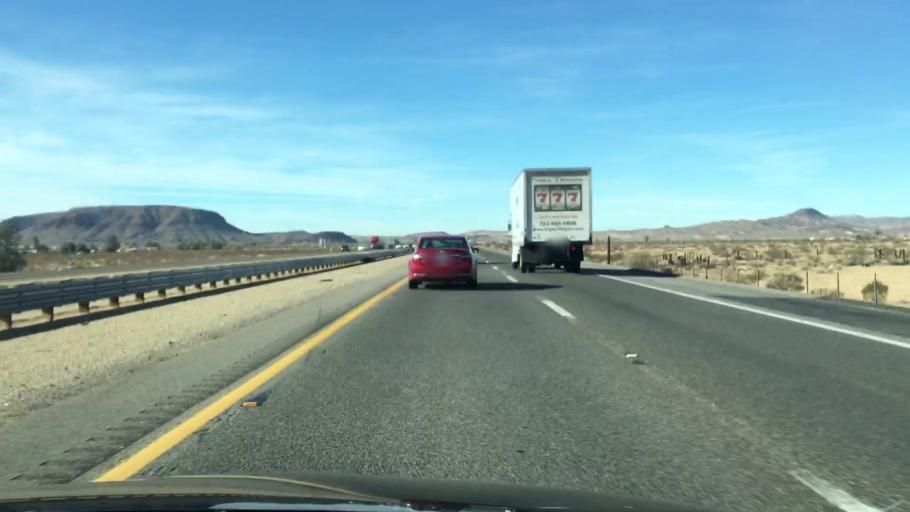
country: US
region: California
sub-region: San Bernardino County
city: Barstow
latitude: 34.9075
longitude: -116.8524
